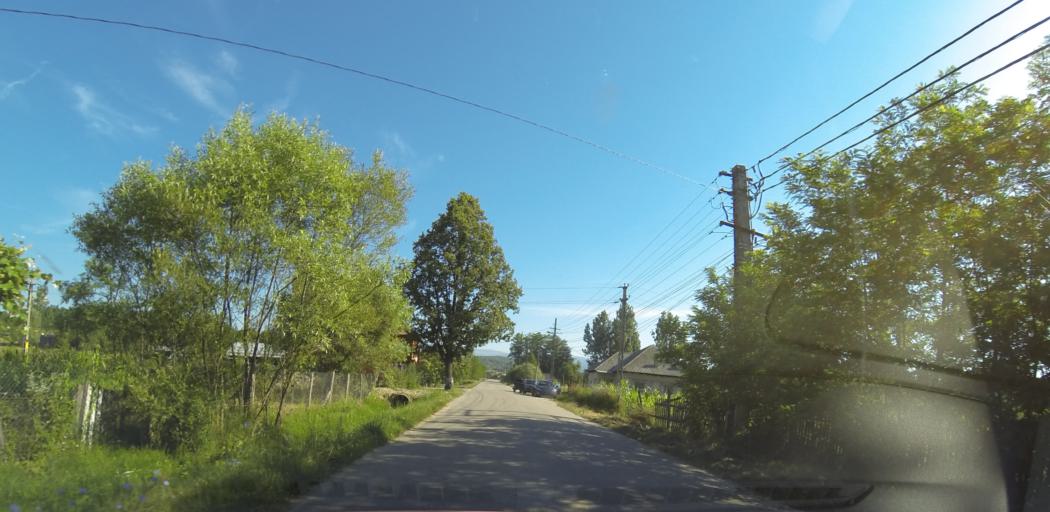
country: RO
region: Valcea
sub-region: Comuna Slatioara
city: Slatioara
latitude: 45.1216
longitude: 23.8902
